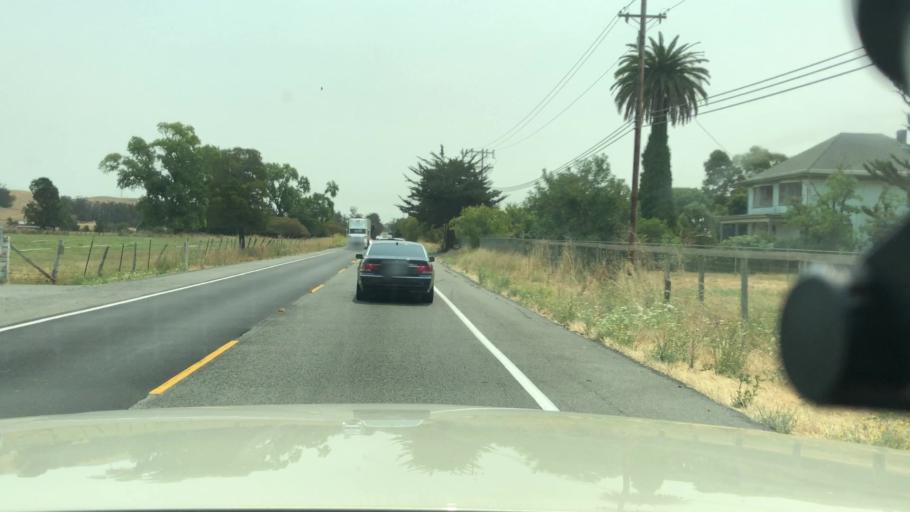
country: US
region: California
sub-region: Sonoma County
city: Petaluma
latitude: 38.2284
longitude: -122.5791
